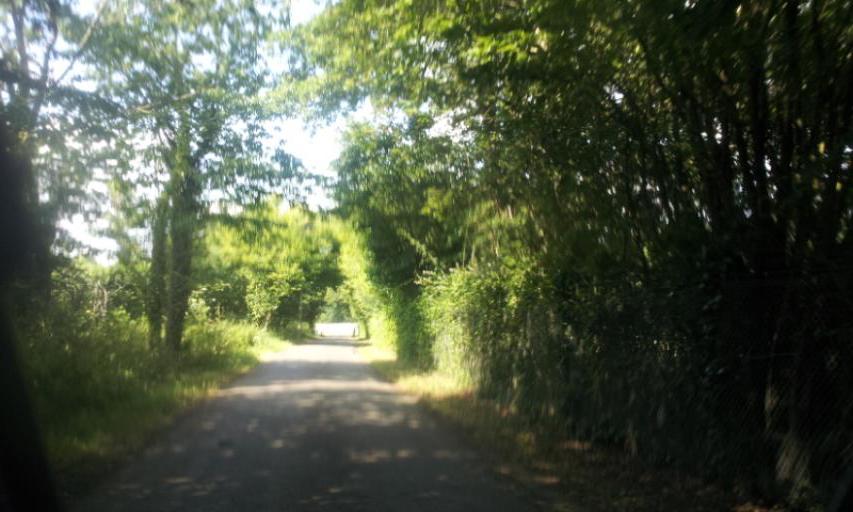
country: GB
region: England
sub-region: Kent
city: Yalding
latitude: 51.2069
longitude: 0.4303
